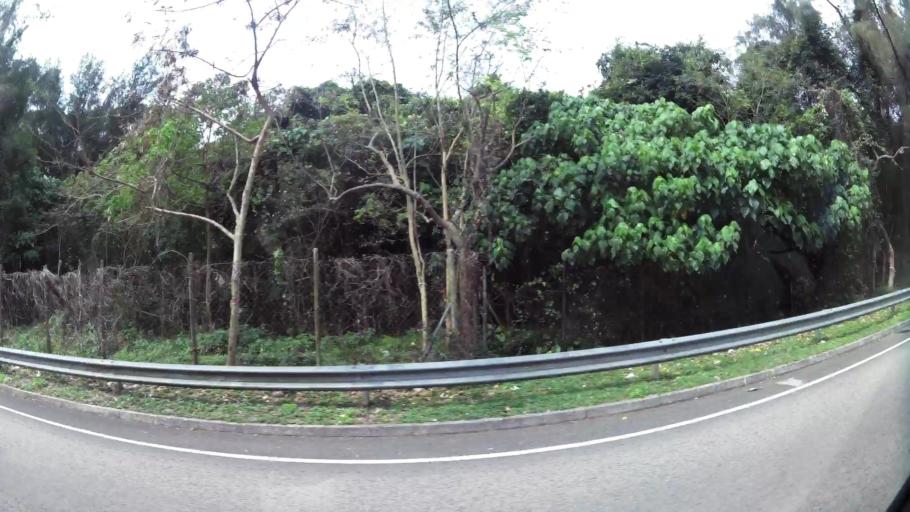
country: HK
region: Wanchai
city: Wan Chai
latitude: 22.2801
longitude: 114.2357
